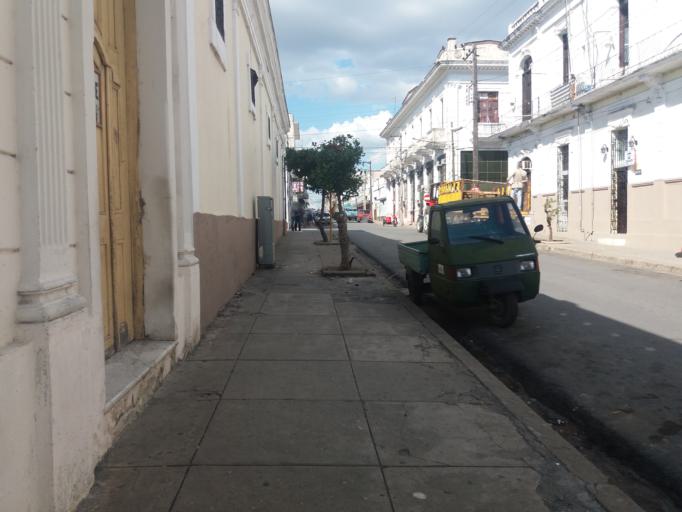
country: CU
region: Cienfuegos
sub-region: Municipio de Cienfuegos
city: Cienfuegos
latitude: 22.1439
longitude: -80.4496
